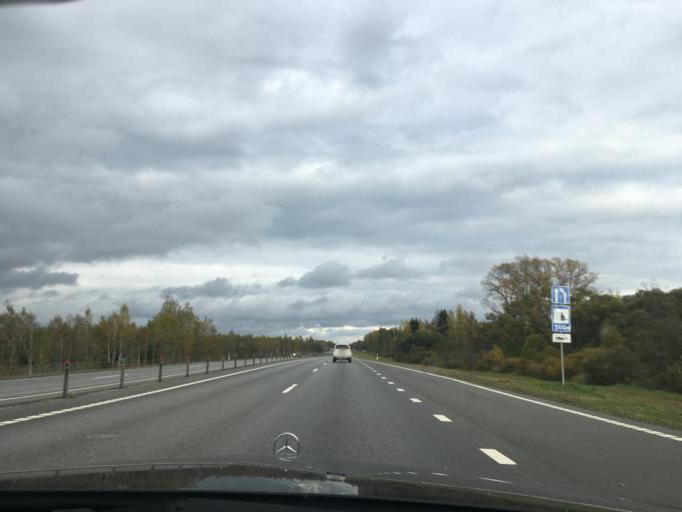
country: BY
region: Vitebsk
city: Dubrowna
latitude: 54.6894
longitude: 30.8944
